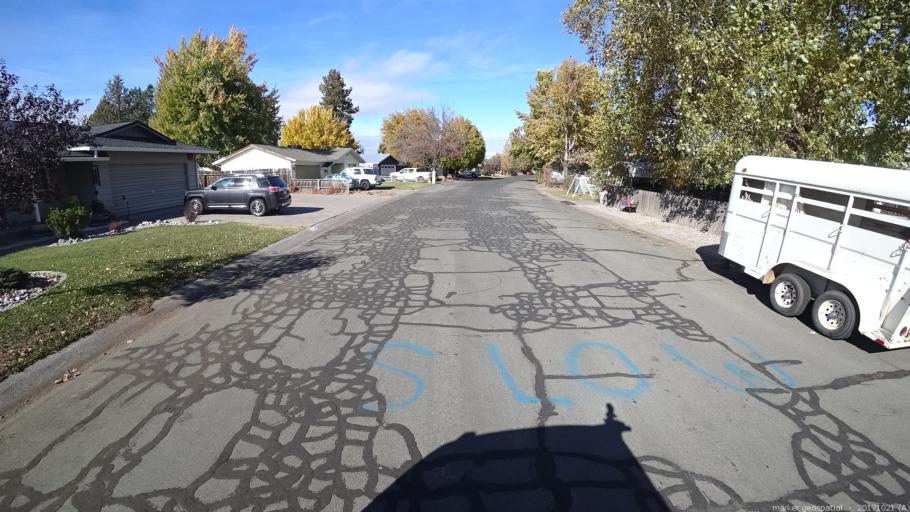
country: US
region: California
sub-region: Shasta County
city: Burney
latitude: 40.8848
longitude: -121.6622
